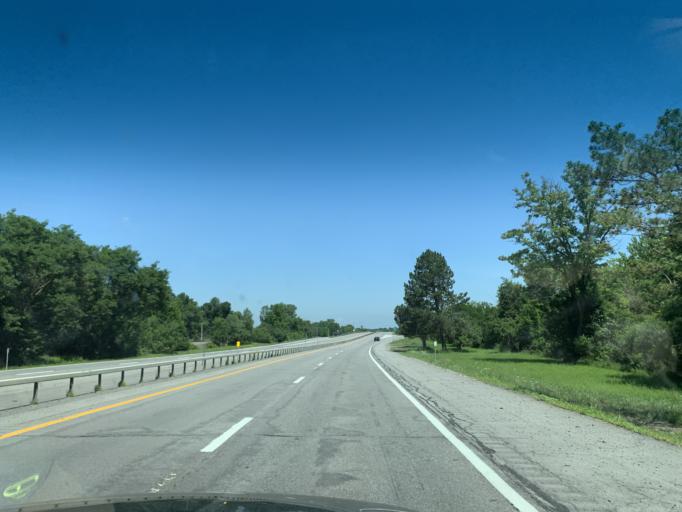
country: US
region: New York
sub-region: Oneida County
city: Washington Mills
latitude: 43.0490
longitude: -75.2747
